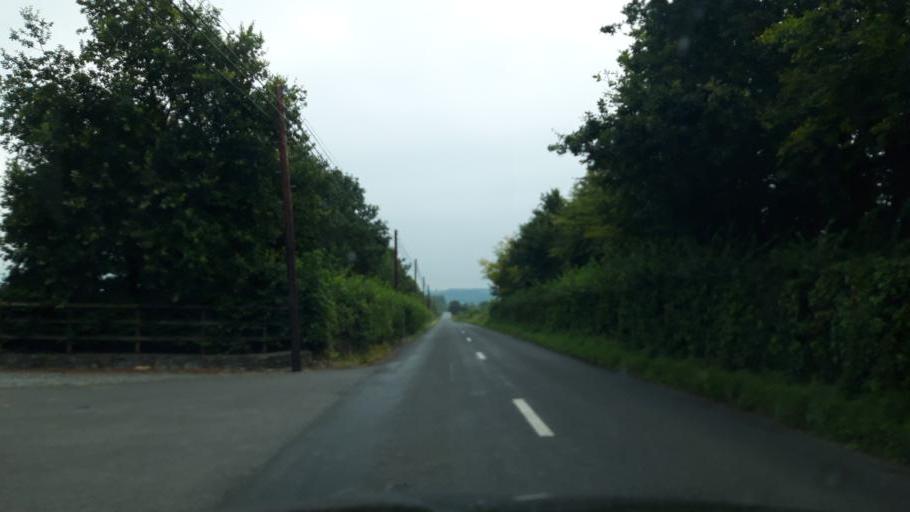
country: IE
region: Munster
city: Fethard
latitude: 52.4810
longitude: -7.6930
